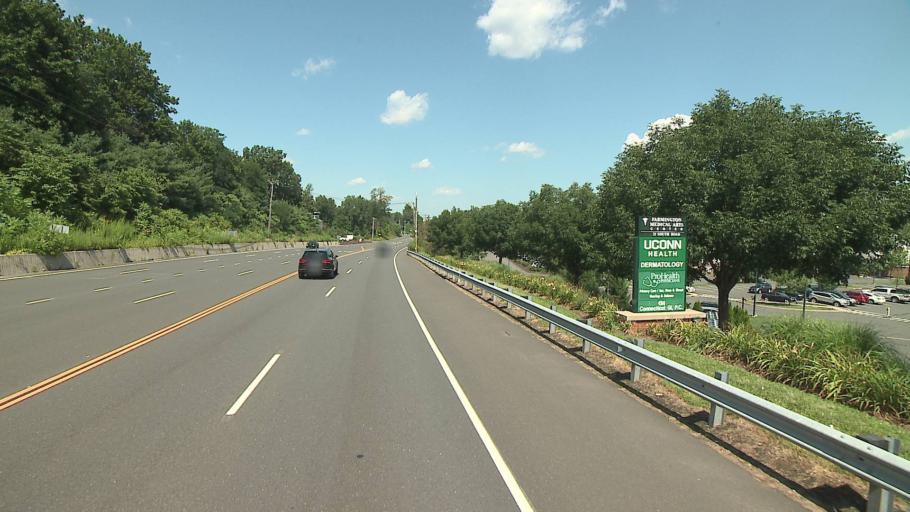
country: US
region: Connecticut
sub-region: Hartford County
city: Farmington
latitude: 41.7284
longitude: -72.8021
